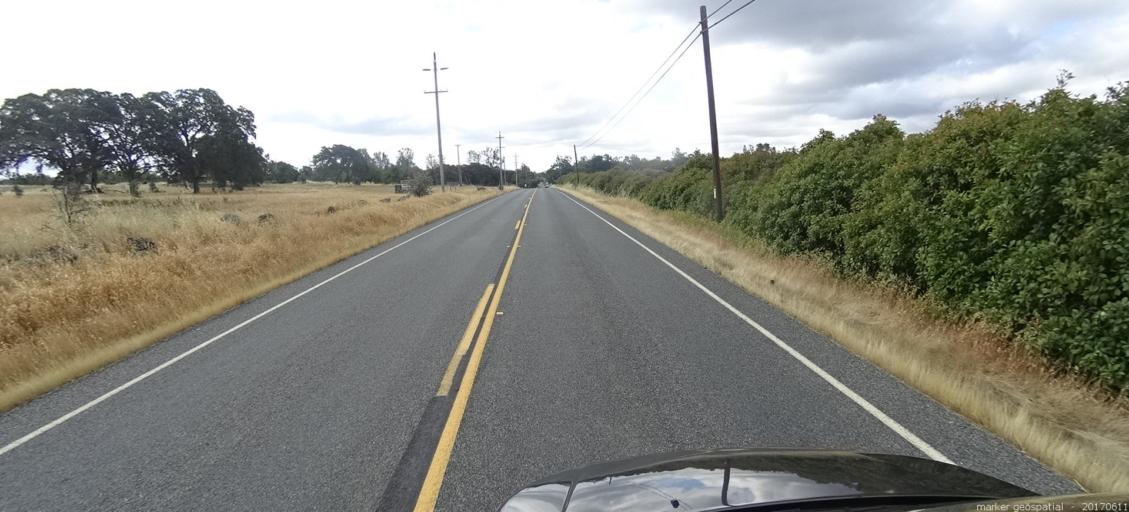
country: US
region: California
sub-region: Yuba County
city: Loma Rica
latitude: 39.3948
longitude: -121.4121
